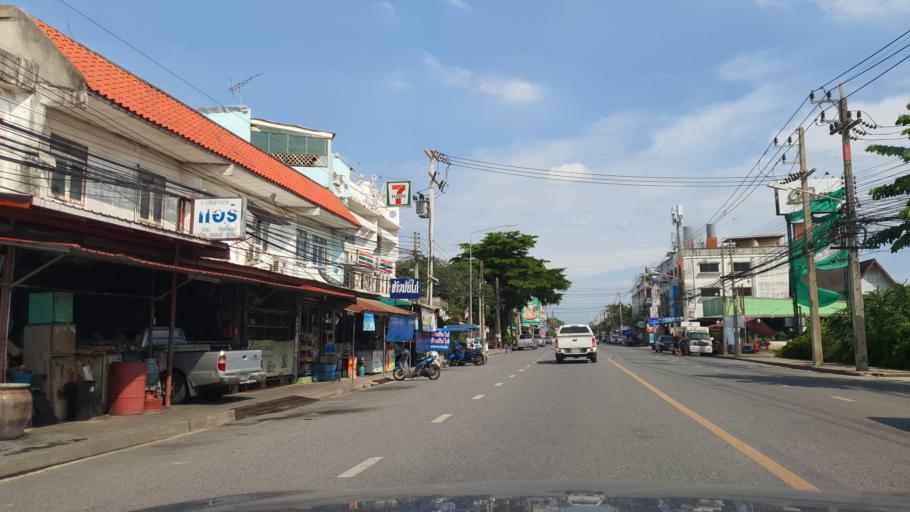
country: TH
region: Chachoengsao
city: Chachoengsao
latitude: 13.6886
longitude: 101.0643
